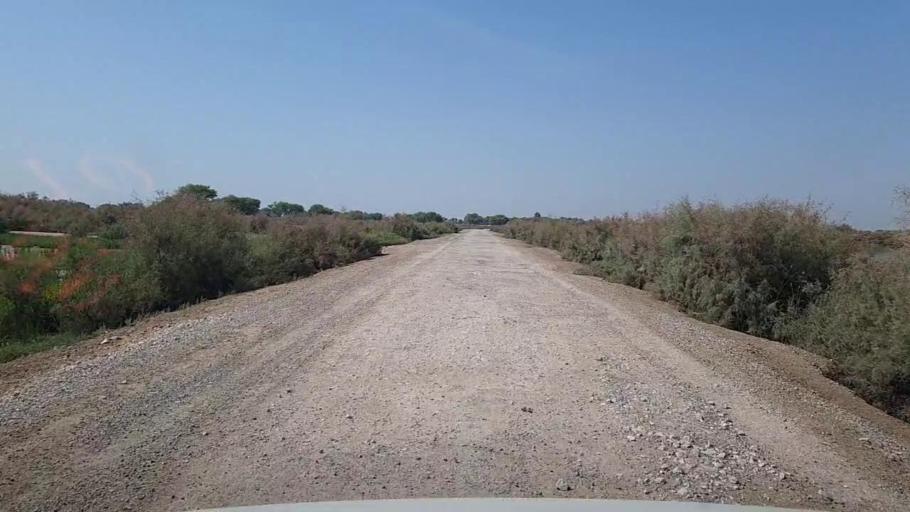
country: PK
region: Sindh
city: Kandhkot
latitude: 28.3357
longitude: 69.3651
